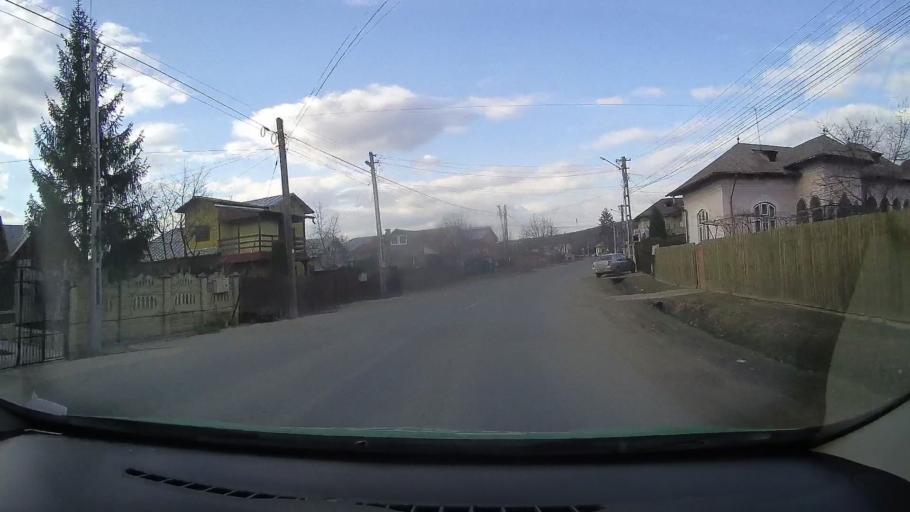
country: RO
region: Dambovita
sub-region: Comuna Gura Ocnitei
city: Gura Ocnitei
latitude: 44.9462
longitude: 25.5596
